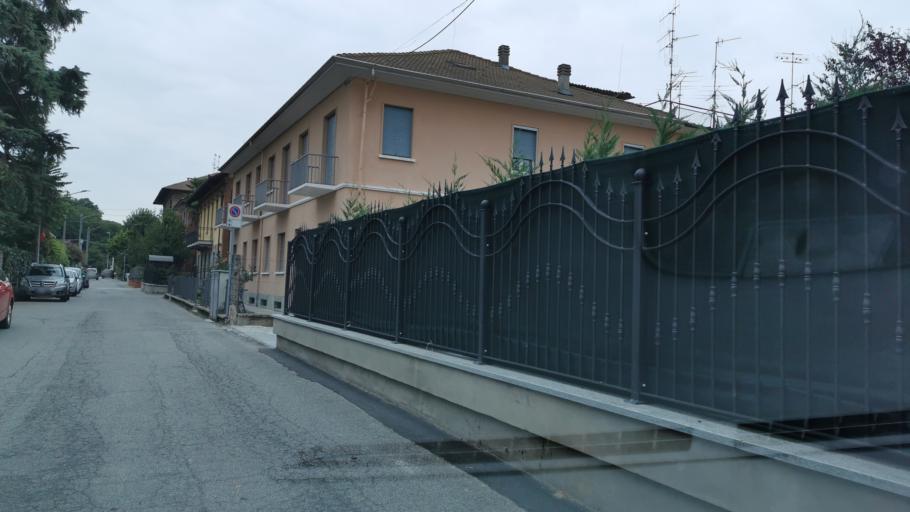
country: IT
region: Piedmont
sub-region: Provincia di Cuneo
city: Bra
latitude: 44.6911
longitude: 7.8558
